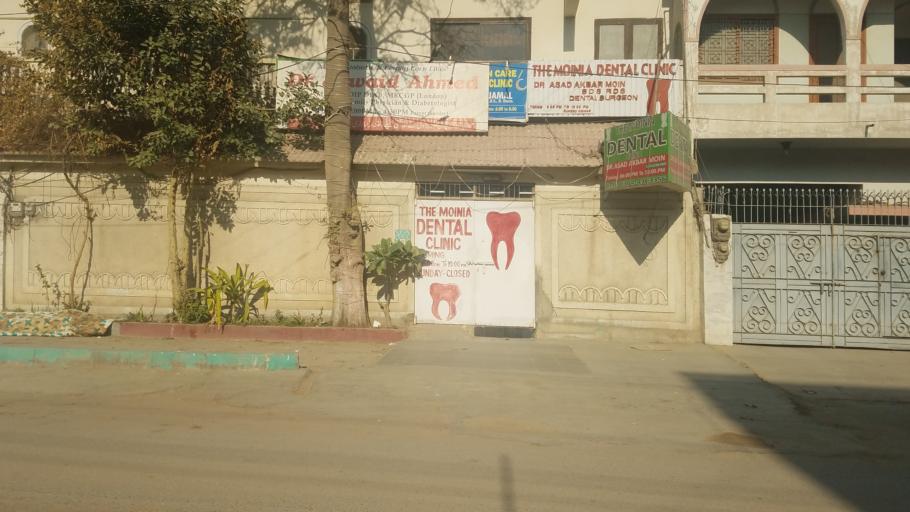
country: PK
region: Sindh
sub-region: Karachi District
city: Karachi
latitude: 24.9398
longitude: 67.0681
